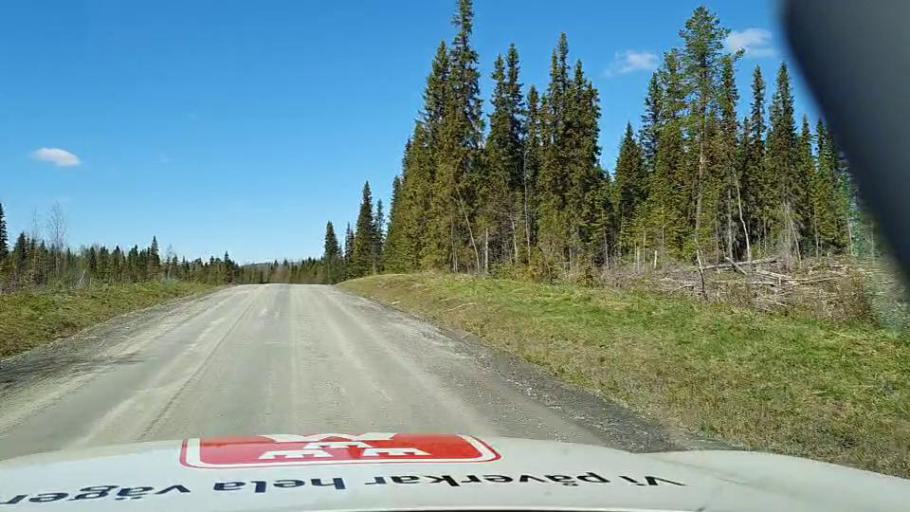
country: SE
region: Jaemtland
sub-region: Krokoms Kommun
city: Valla
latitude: 63.6597
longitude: 13.7594
